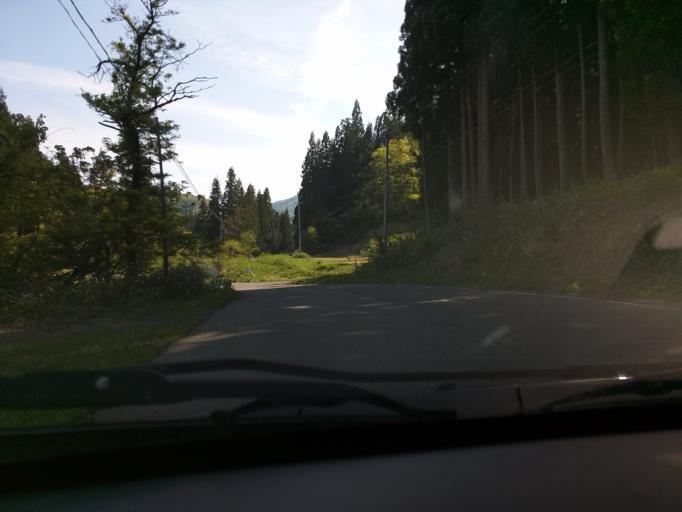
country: JP
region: Fukushima
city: Kitakata
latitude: 37.5645
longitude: 139.6303
